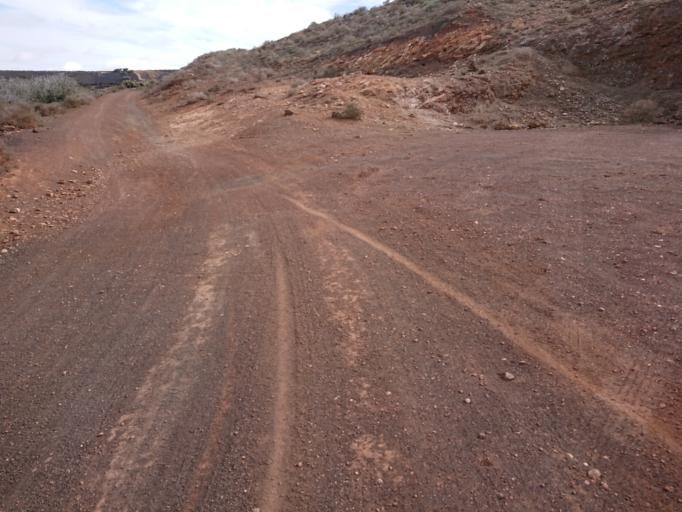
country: ES
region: Canary Islands
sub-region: Provincia de Las Palmas
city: Tinajo
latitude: 29.0206
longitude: -13.6780
